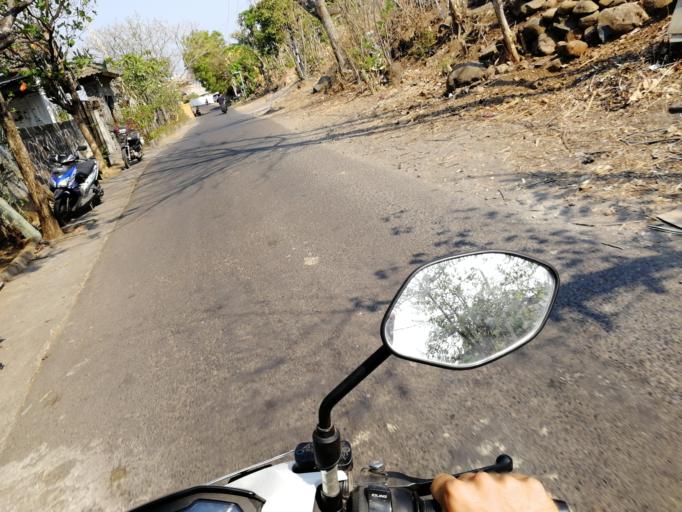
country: ID
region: Bali
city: Biaslantang Kaler
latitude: -8.3583
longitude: 115.6963
